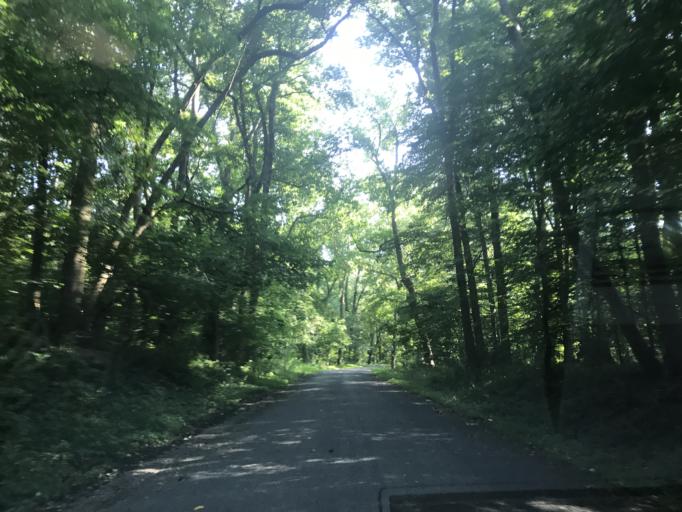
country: US
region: Maryland
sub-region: Harford County
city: Aberdeen
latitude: 39.5212
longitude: -76.1241
